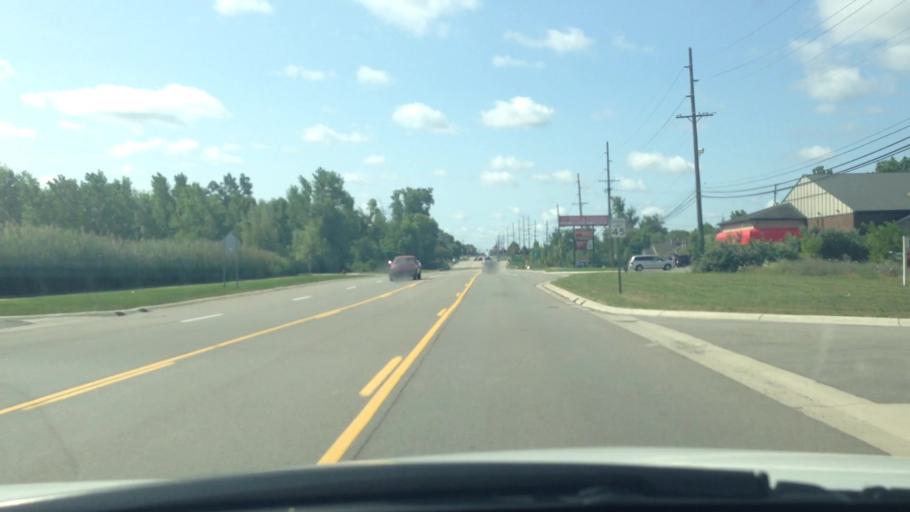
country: US
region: Michigan
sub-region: Oakland County
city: Wolverine Lake
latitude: 42.5648
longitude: -83.4396
